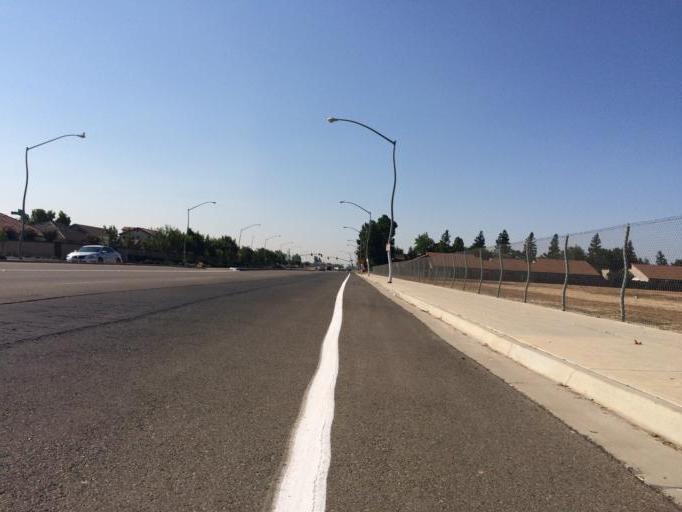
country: US
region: California
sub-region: Fresno County
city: Tarpey Village
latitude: 36.7821
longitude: -119.6823
